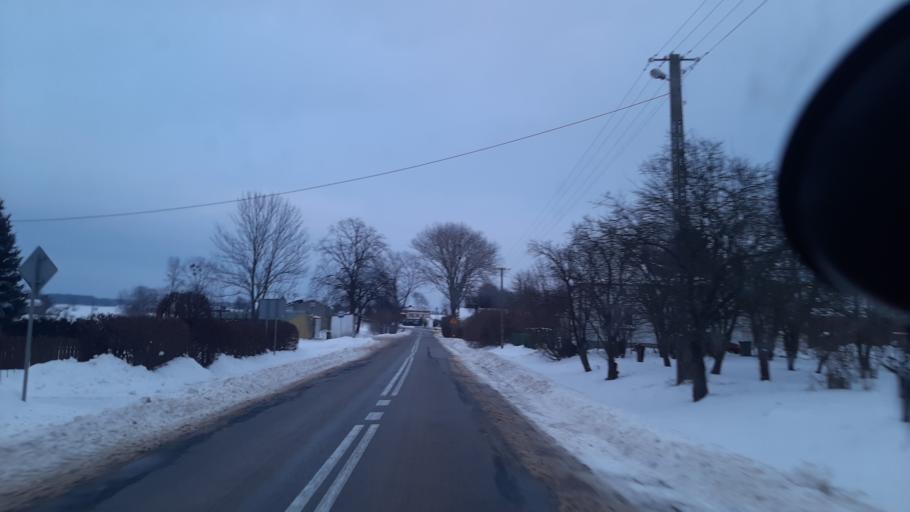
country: PL
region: Lublin Voivodeship
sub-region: Powiat lubelski
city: Jastkow
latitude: 51.3436
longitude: 22.4069
